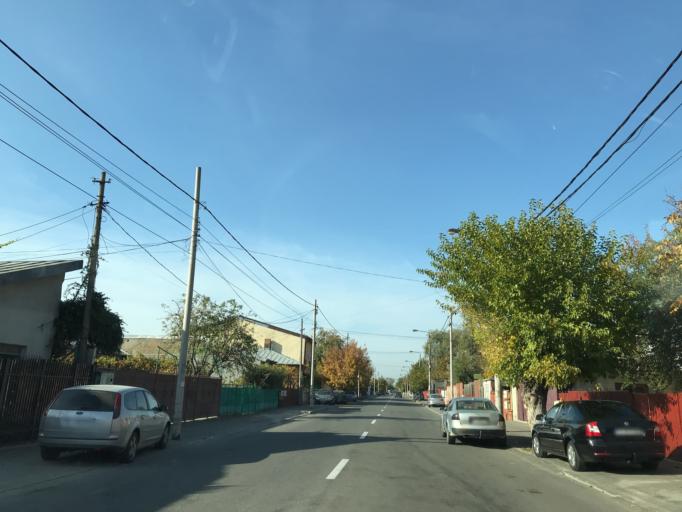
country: RO
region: Olt
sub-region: Municipiul Slatina
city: Slatina
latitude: 44.4343
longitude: 24.3508
